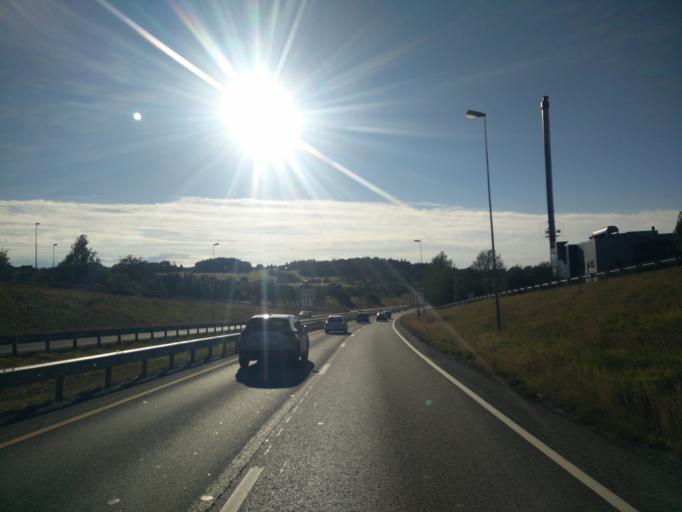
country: NO
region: Sor-Trondelag
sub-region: Klaebu
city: Klaebu
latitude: 63.4225
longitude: 10.5325
